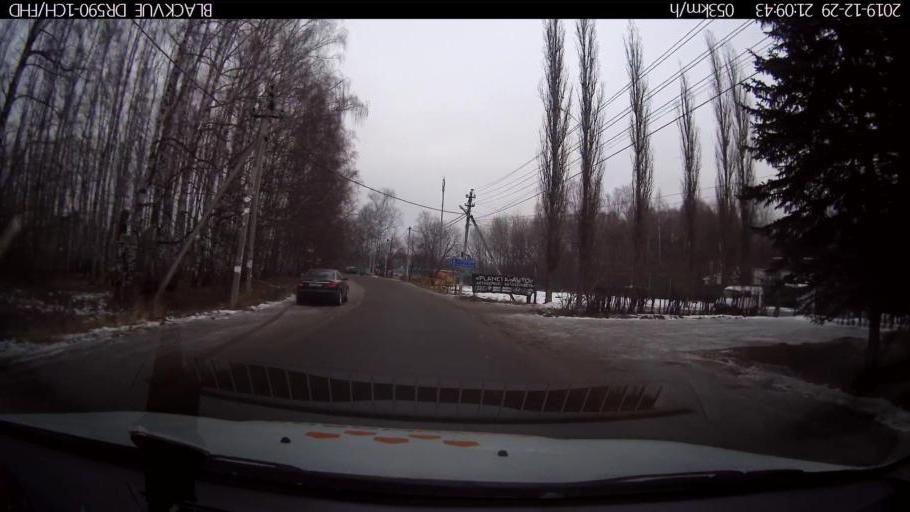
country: RU
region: Nizjnij Novgorod
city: Afonino
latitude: 56.2176
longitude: 44.0357
